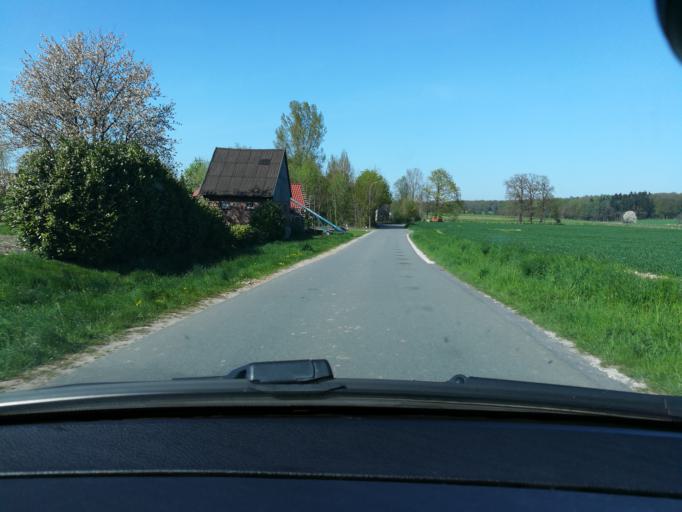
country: DE
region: North Rhine-Westphalia
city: Borgholzhausen
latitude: 52.1015
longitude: 8.3388
